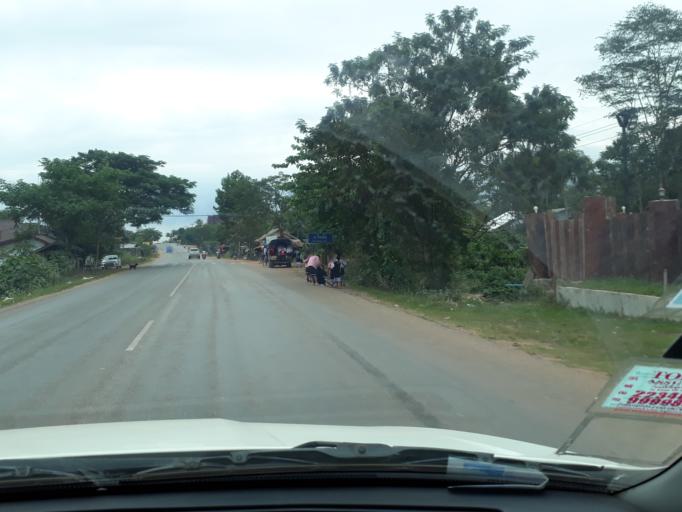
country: LA
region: Vientiane
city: Muang Phon-Hong
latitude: 18.3253
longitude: 102.4476
